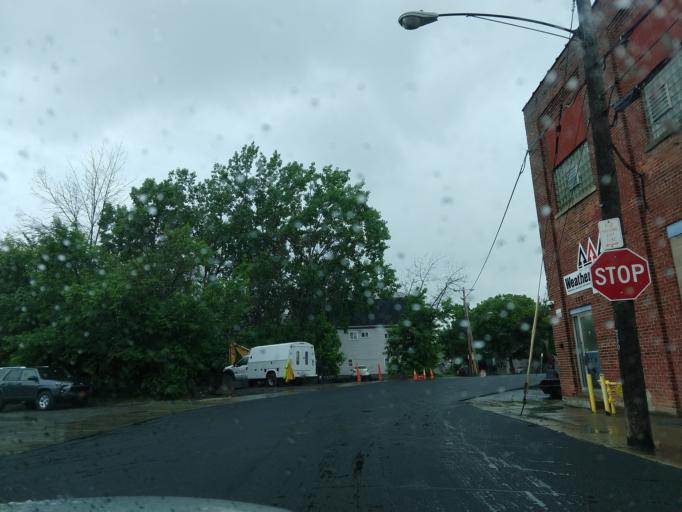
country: US
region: New York
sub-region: Erie County
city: Kenmore
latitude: 42.9423
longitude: -78.8805
